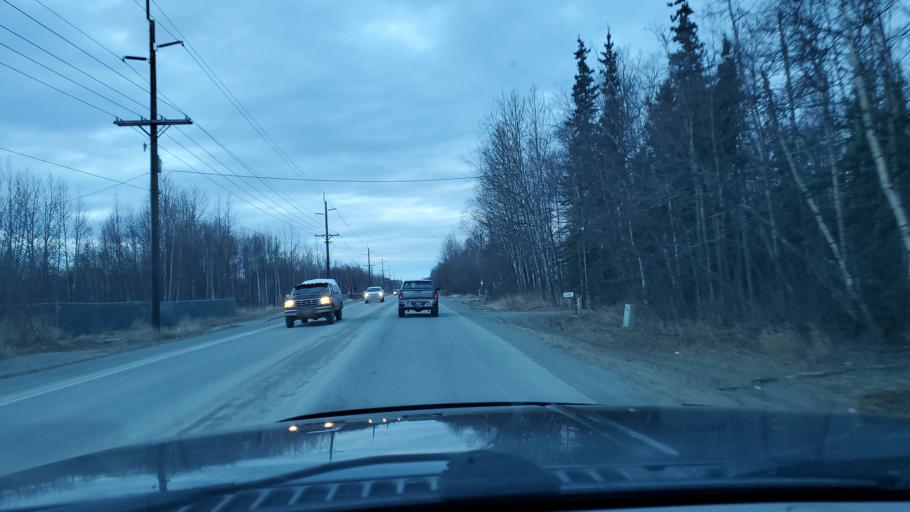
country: US
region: Alaska
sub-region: Matanuska-Susitna Borough
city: Lakes
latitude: 61.6139
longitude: -149.3128
